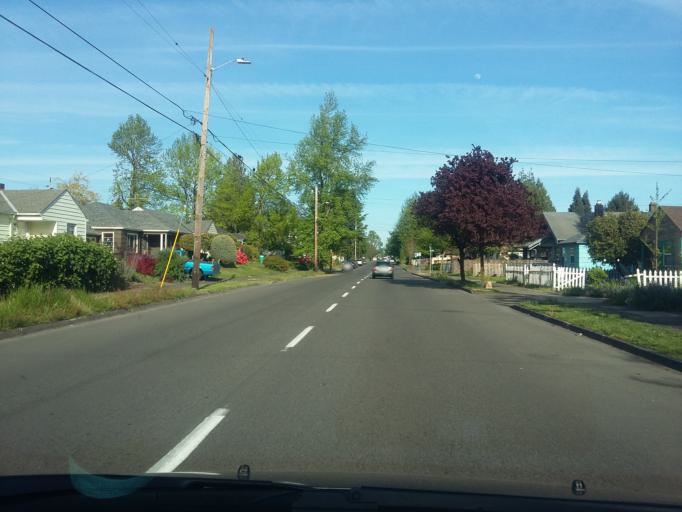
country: US
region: Oregon
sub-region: Multnomah County
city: Lents
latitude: 45.5184
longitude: -122.5742
